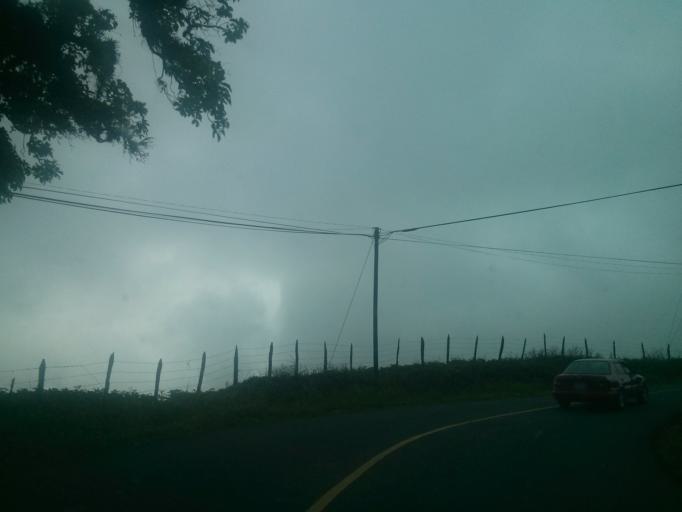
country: CR
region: Cartago
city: Cot
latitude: 9.9128
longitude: -83.8016
